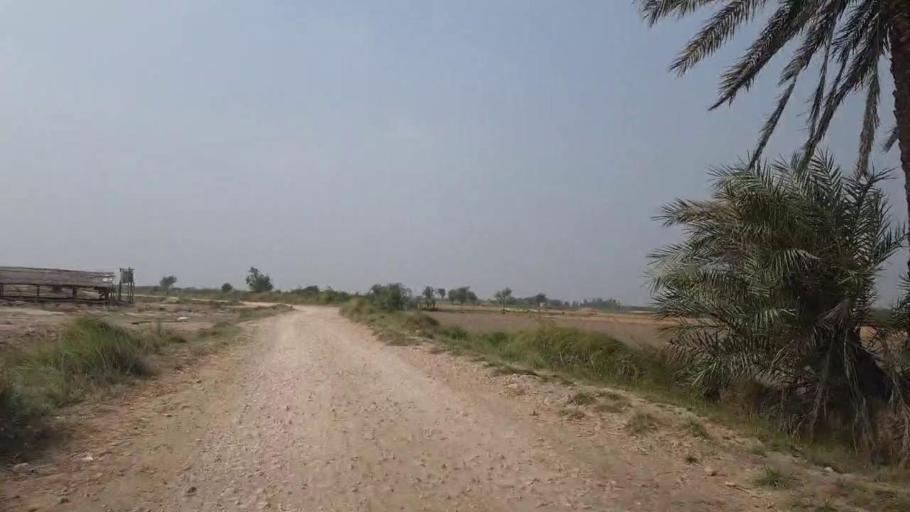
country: PK
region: Sindh
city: Kario
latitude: 24.8778
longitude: 68.5063
